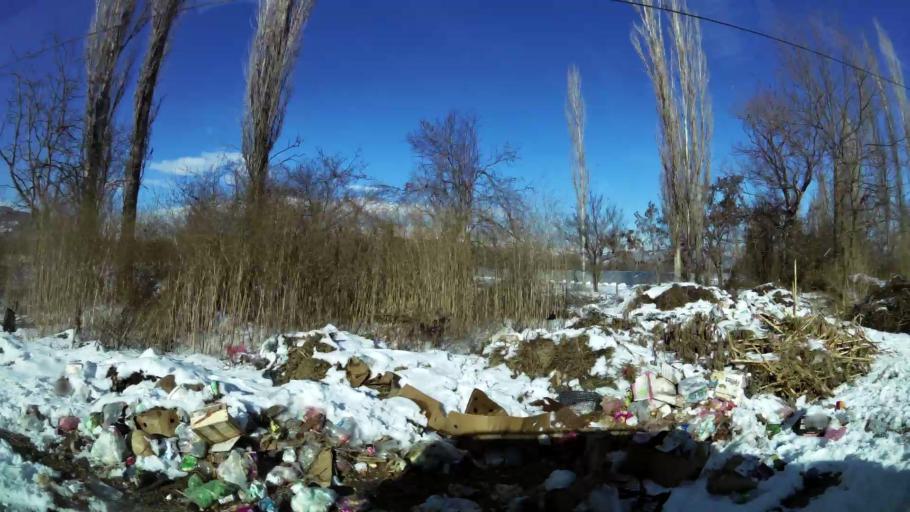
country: MK
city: Grchec
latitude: 41.9814
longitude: 21.3220
